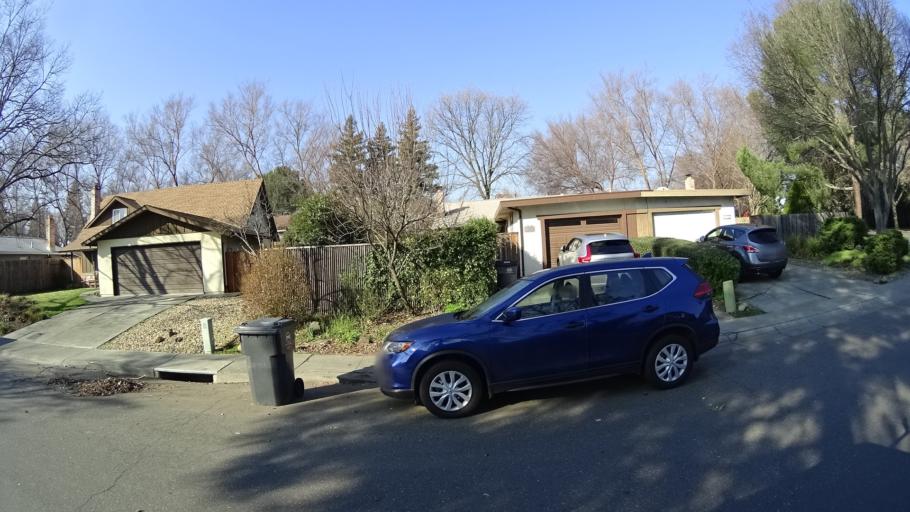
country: US
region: California
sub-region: Yolo County
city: Davis
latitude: 38.5537
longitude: -121.7851
